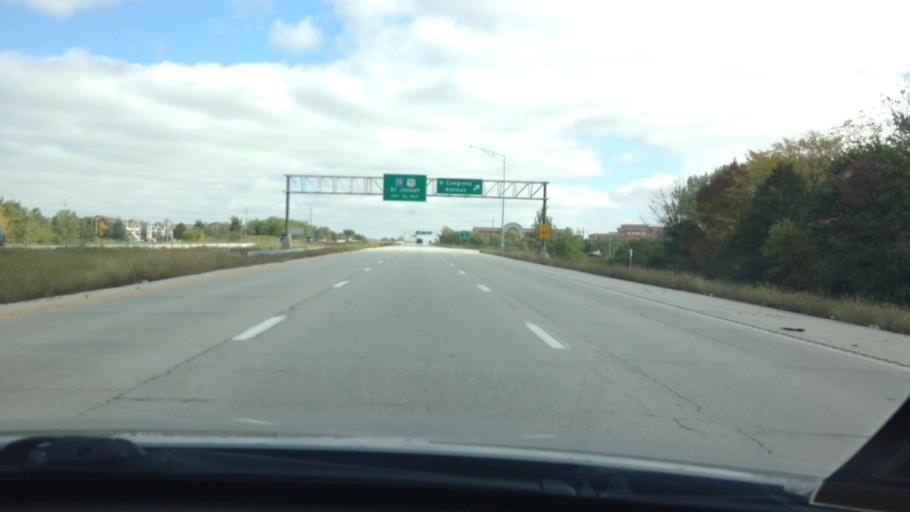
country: US
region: Missouri
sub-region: Platte County
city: Weatherby Lake
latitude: 39.2542
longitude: -94.6729
